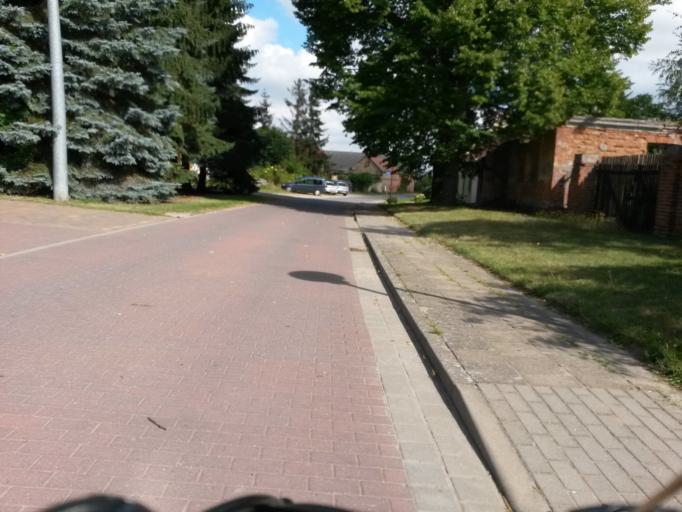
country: DE
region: Brandenburg
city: Angermunde
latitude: 53.0701
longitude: 14.0024
